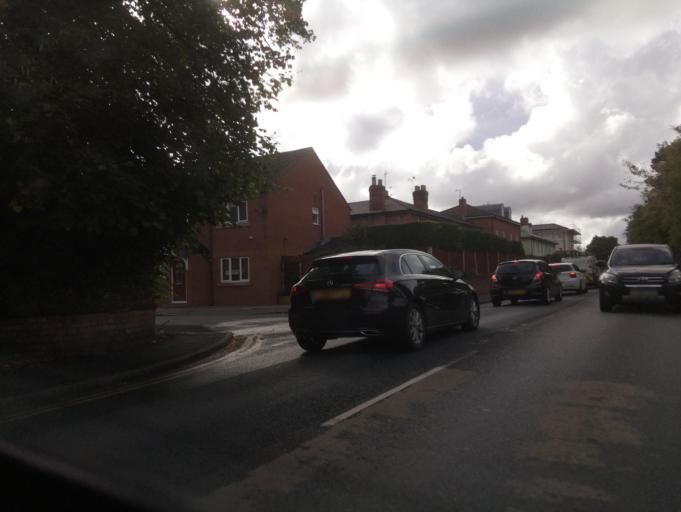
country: GB
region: England
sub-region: Worcestershire
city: Kidderminster
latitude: 52.3845
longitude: -2.2358
